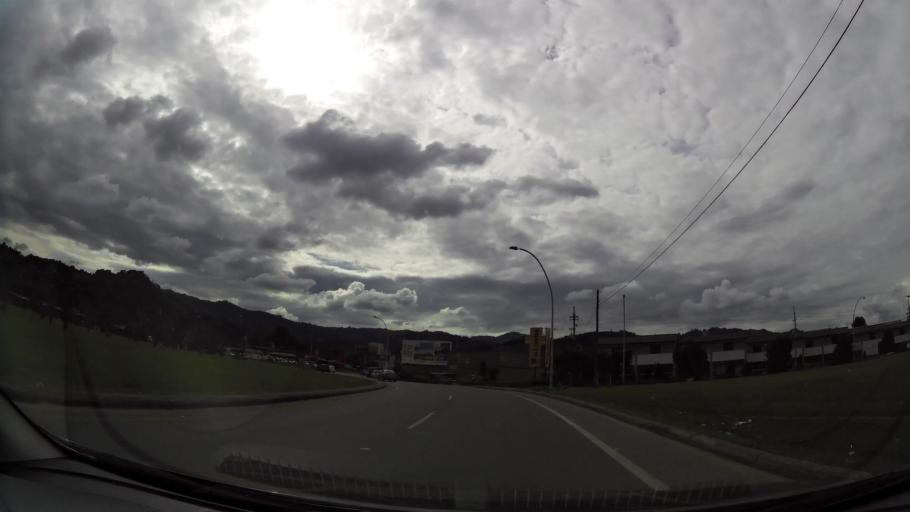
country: CO
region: Antioquia
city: Rionegro
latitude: 6.1768
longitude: -75.4357
